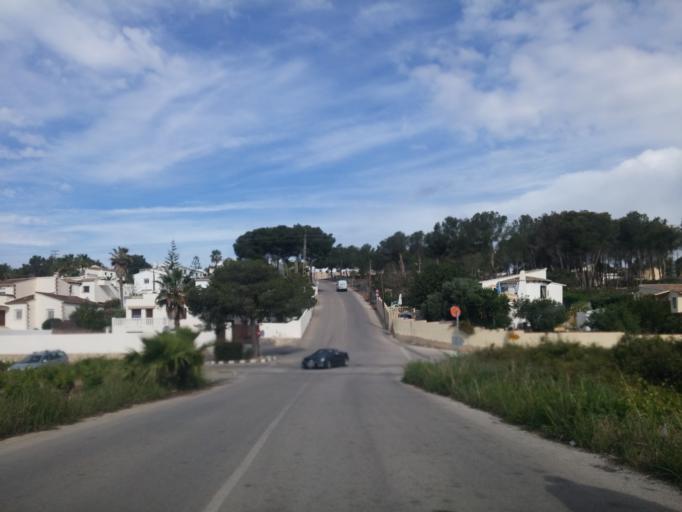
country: ES
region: Valencia
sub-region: Provincia de Alicante
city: Moraira
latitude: 38.6980
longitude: 0.1310
